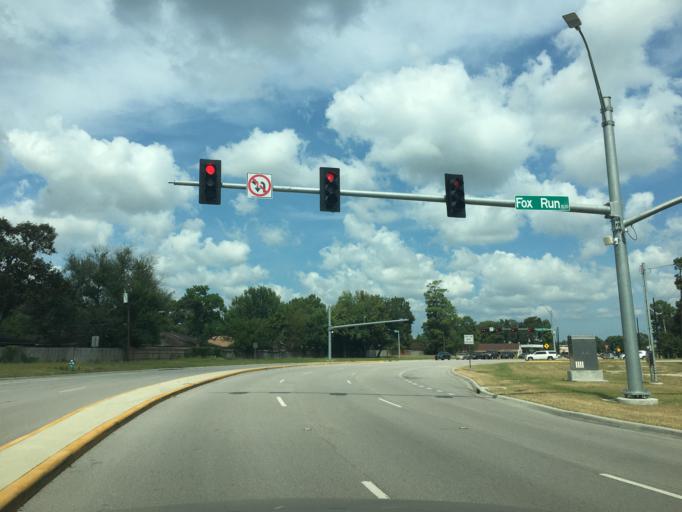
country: US
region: Texas
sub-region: Harris County
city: Spring
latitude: 30.1171
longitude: -95.3962
